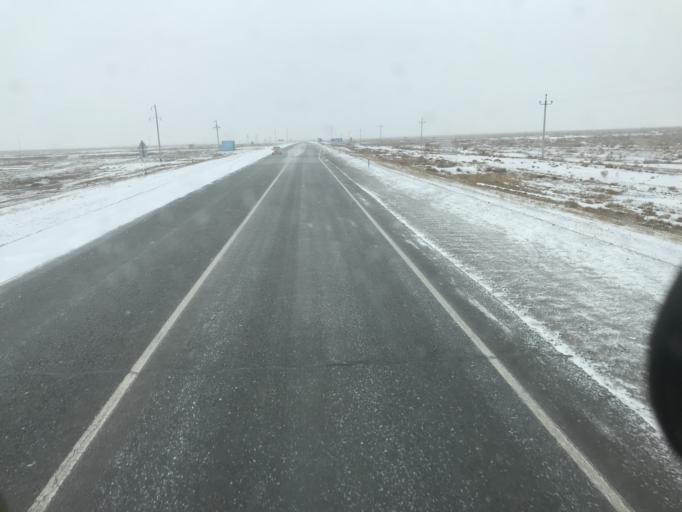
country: KZ
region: Qyzylorda
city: Zhosaly
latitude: 45.4436
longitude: 64.0718
